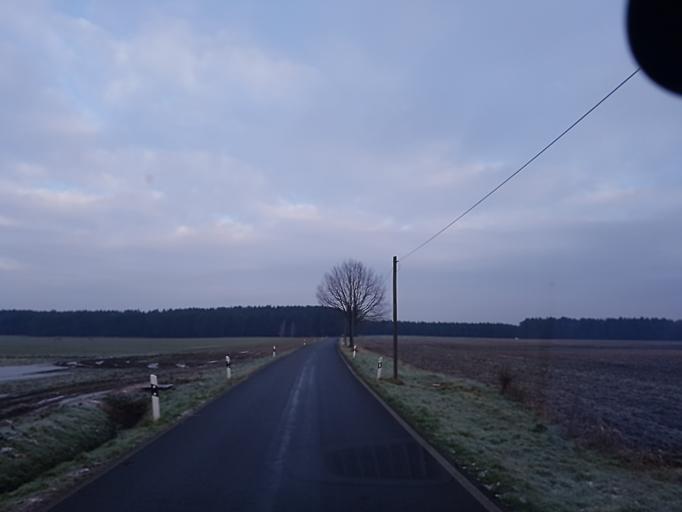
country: DE
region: Brandenburg
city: Crinitz
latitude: 51.7363
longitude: 13.8300
